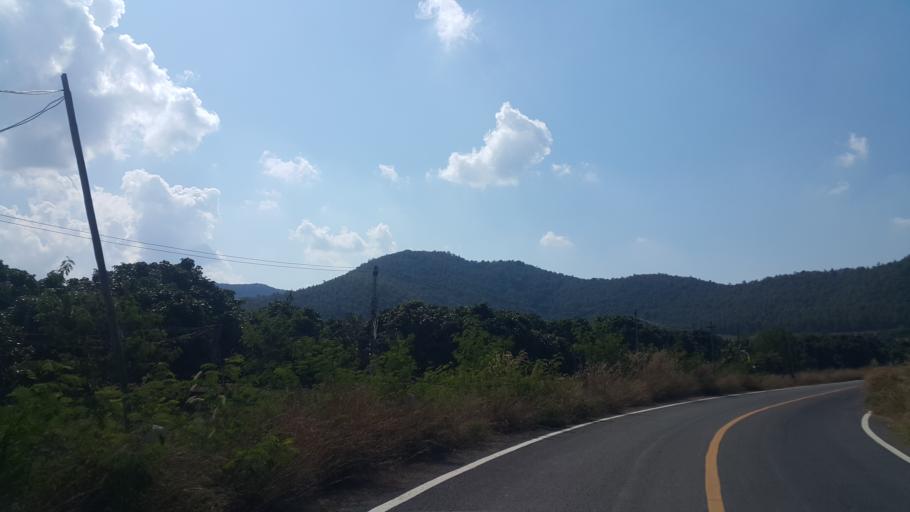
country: TH
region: Lamphun
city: Ban Thi
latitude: 18.6224
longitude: 99.1515
